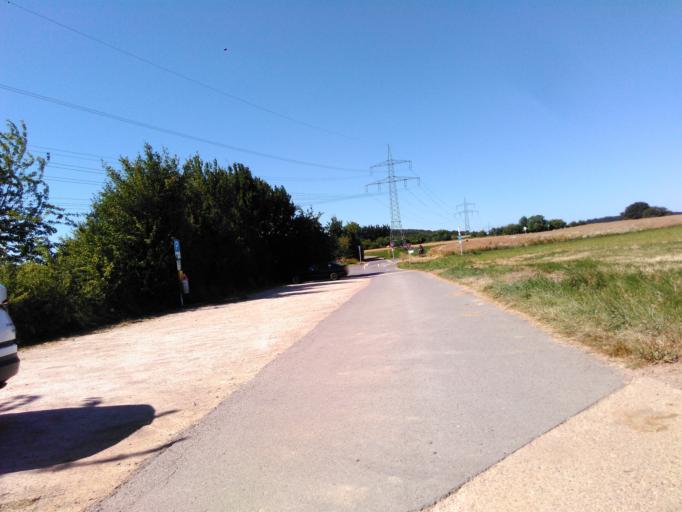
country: LU
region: Luxembourg
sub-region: Canton d'Esch-sur-Alzette
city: Reckange-sur-Mess
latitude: 49.5658
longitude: 6.0289
